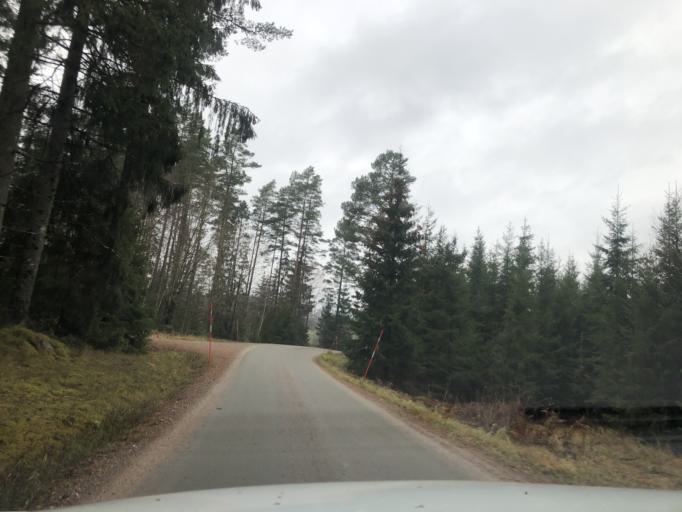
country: SE
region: Vaestra Goetaland
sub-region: Ulricehamns Kommun
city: Ulricehamn
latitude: 57.8557
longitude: 13.6274
